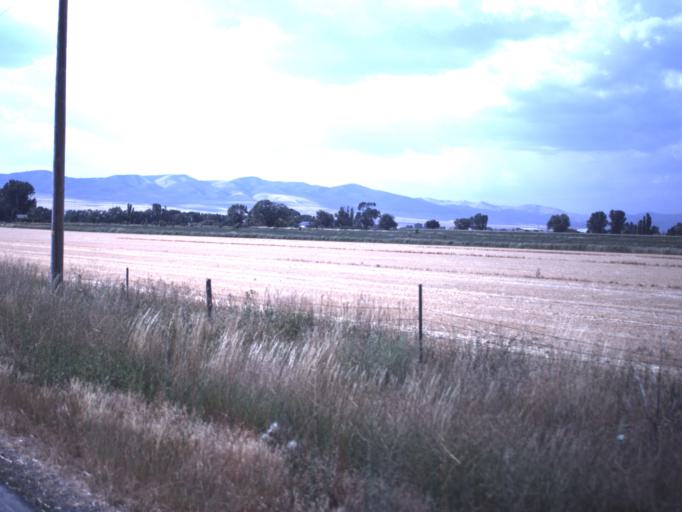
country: US
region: Utah
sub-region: Box Elder County
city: Garland
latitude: 41.7927
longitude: -112.1190
